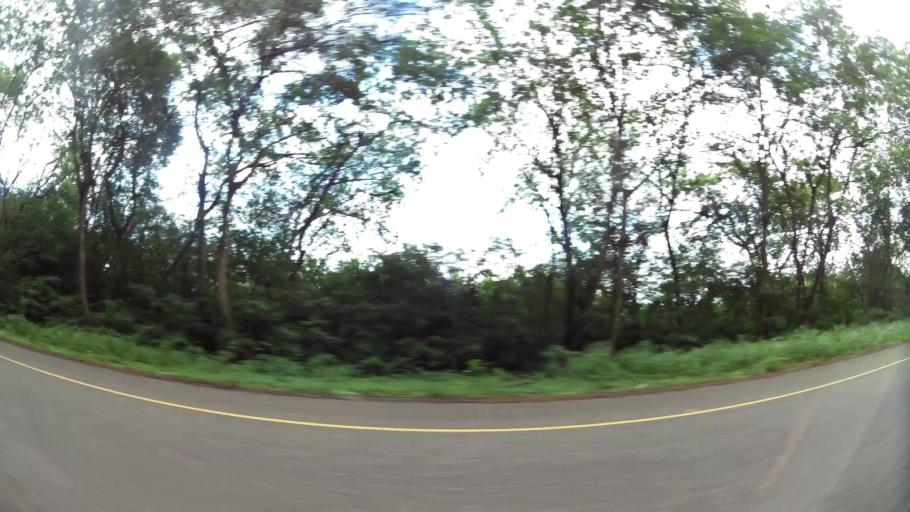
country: DO
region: Monsenor Nouel
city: Sabana del Puerto
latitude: 19.0957
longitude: -70.4383
